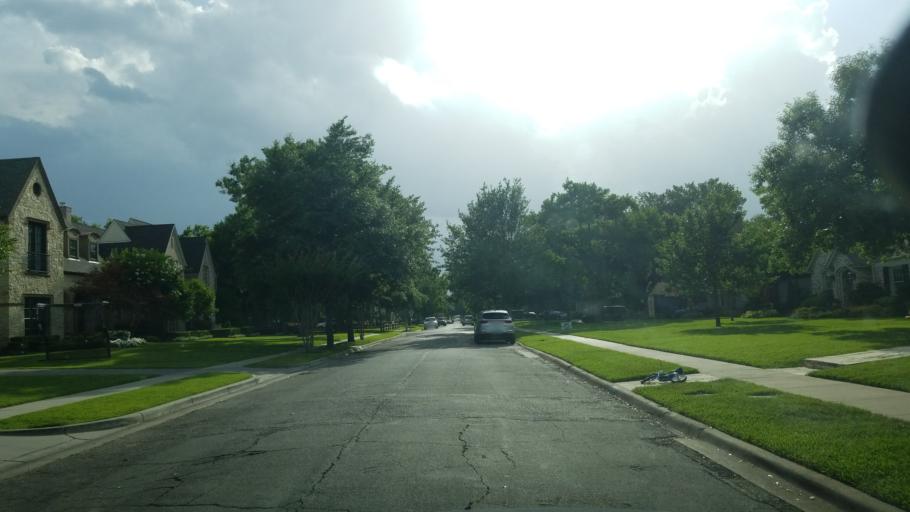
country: US
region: Texas
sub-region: Dallas County
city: University Park
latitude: 32.8560
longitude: -96.7723
